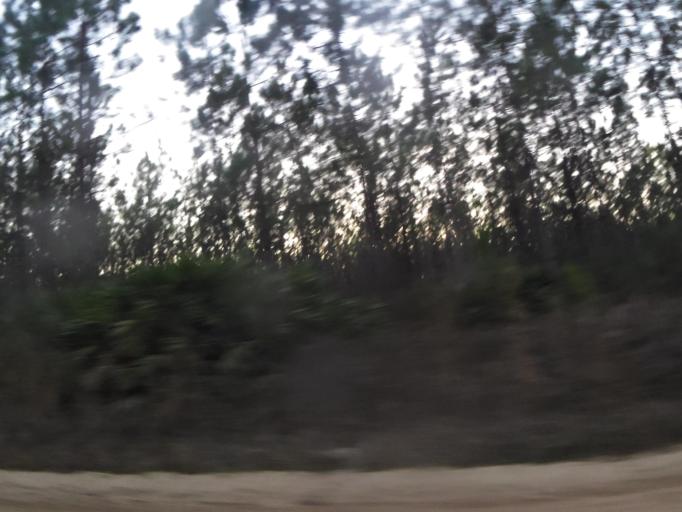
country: US
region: Florida
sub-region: Clay County
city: Asbury Lake
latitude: 29.9465
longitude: -81.7881
